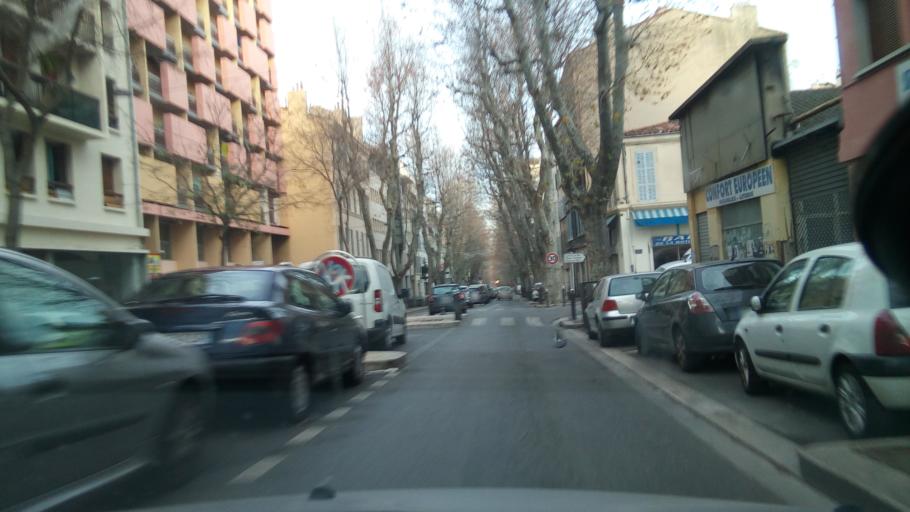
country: FR
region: Provence-Alpes-Cote d'Azur
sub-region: Departement des Bouches-du-Rhone
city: Marseille 01
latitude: 43.3064
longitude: 5.3842
